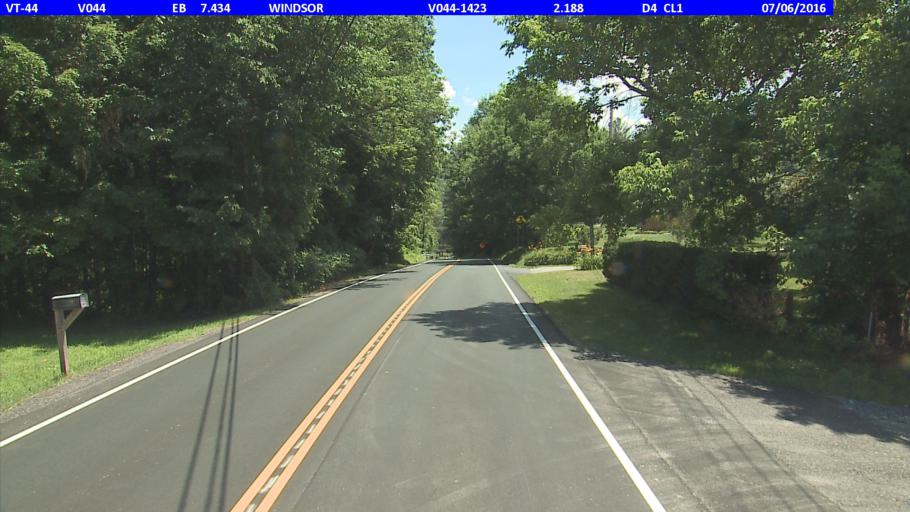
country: US
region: Vermont
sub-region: Windsor County
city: Windsor
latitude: 43.4561
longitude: -72.4135
